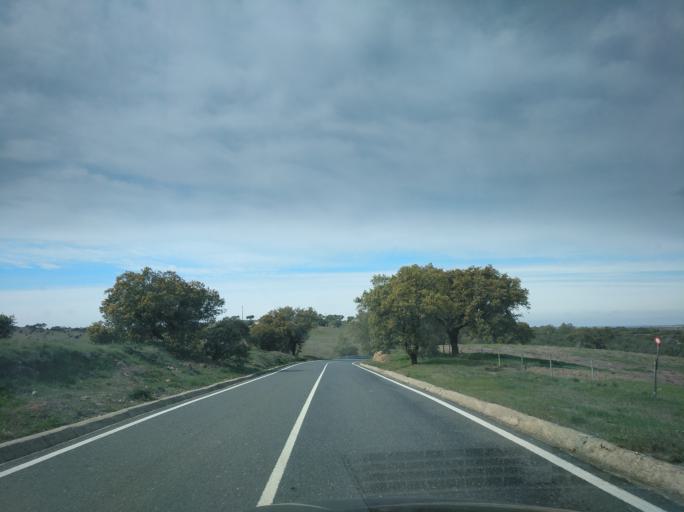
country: PT
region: Beja
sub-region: Mertola
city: Mertola
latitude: 37.7187
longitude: -7.7584
